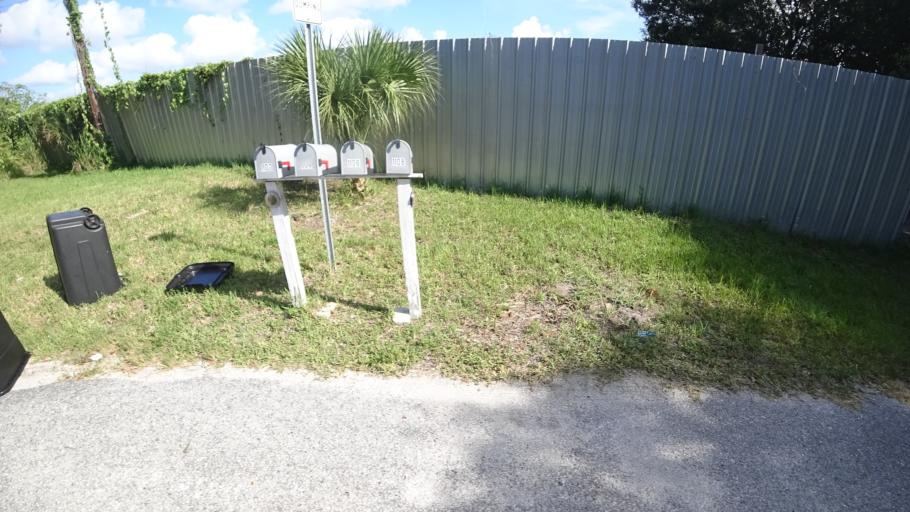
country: US
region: Florida
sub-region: Manatee County
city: West Samoset
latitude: 27.4431
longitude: -82.5514
